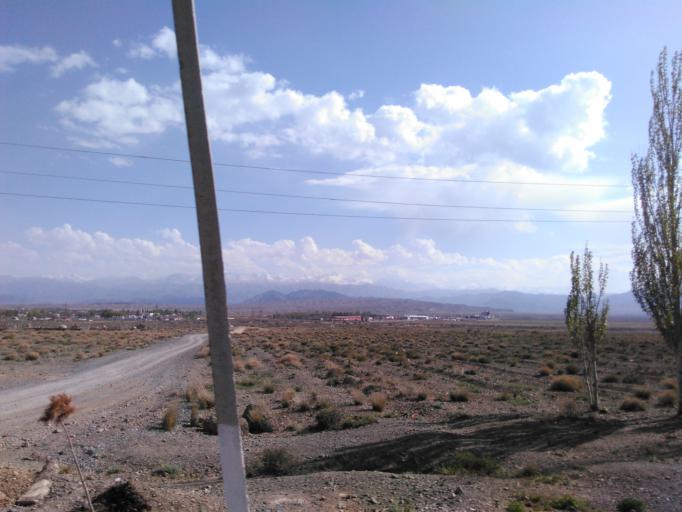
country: KG
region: Ysyk-Koel
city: Balykchy
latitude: 42.4557
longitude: 76.1494
